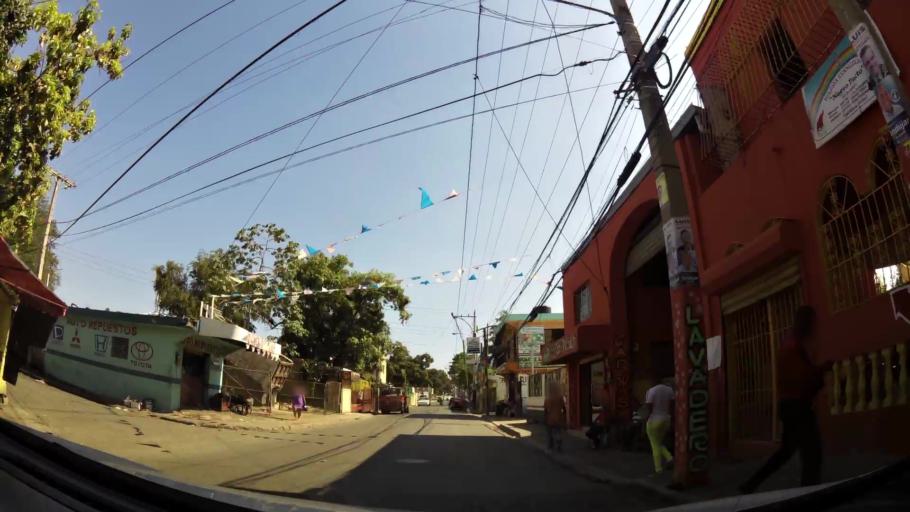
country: DO
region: Santo Domingo
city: Santo Domingo Oeste
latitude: 18.4707
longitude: -69.9992
